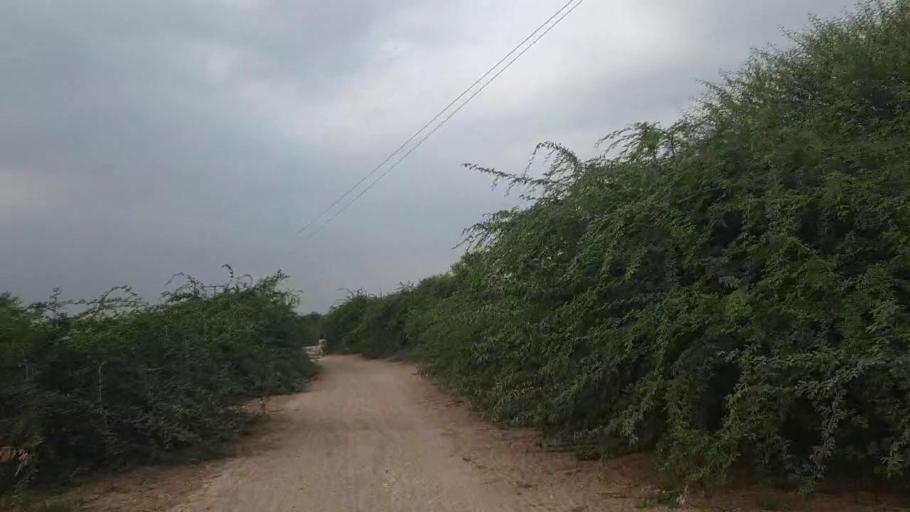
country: PK
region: Sindh
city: Badin
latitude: 24.6138
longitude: 68.6856
